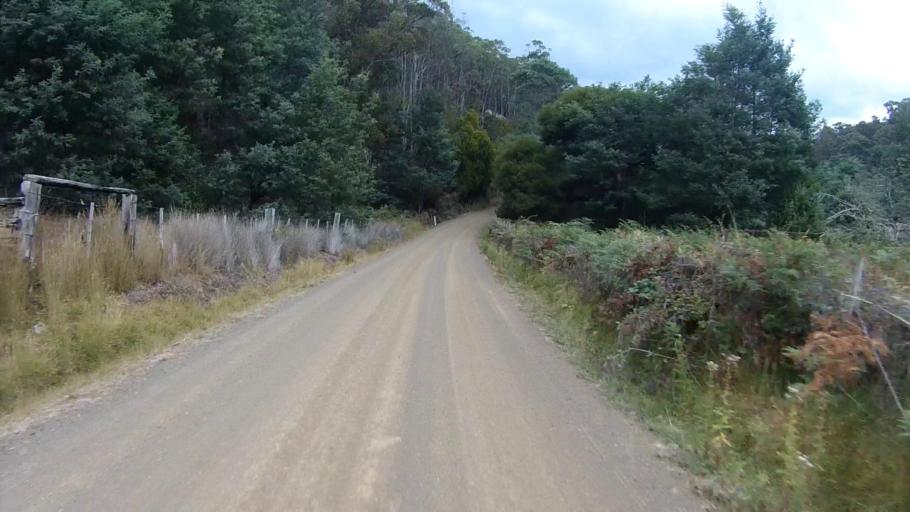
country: AU
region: Tasmania
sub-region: Huon Valley
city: Cygnet
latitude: -43.2259
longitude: 147.1689
